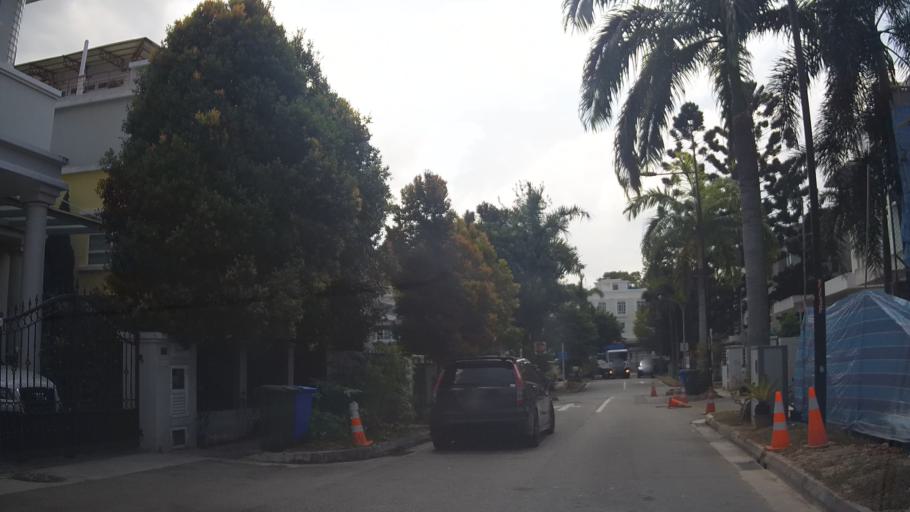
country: SG
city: Singapore
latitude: 1.3192
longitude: 103.9525
